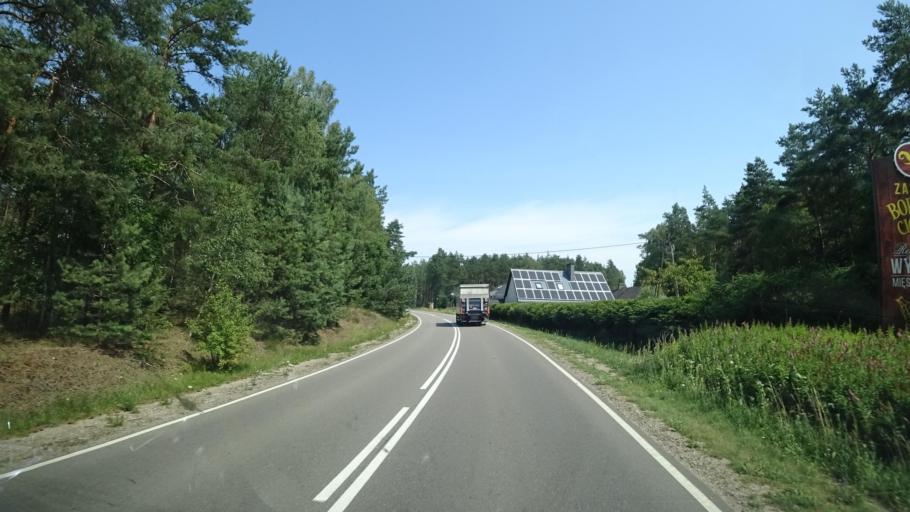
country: PL
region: Pomeranian Voivodeship
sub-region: Powiat koscierski
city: Lipusz
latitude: 54.0975
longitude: 17.8135
